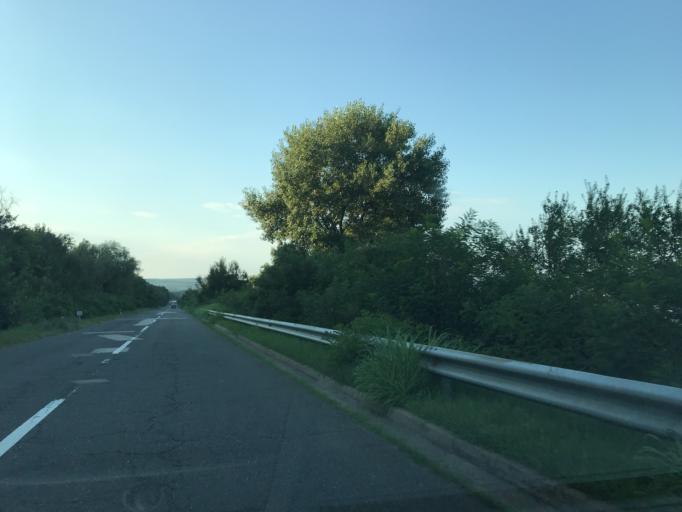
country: RO
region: Mehedinti
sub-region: Comuna Gogosu
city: Ostrovu Mare
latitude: 44.4539
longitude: 22.4527
